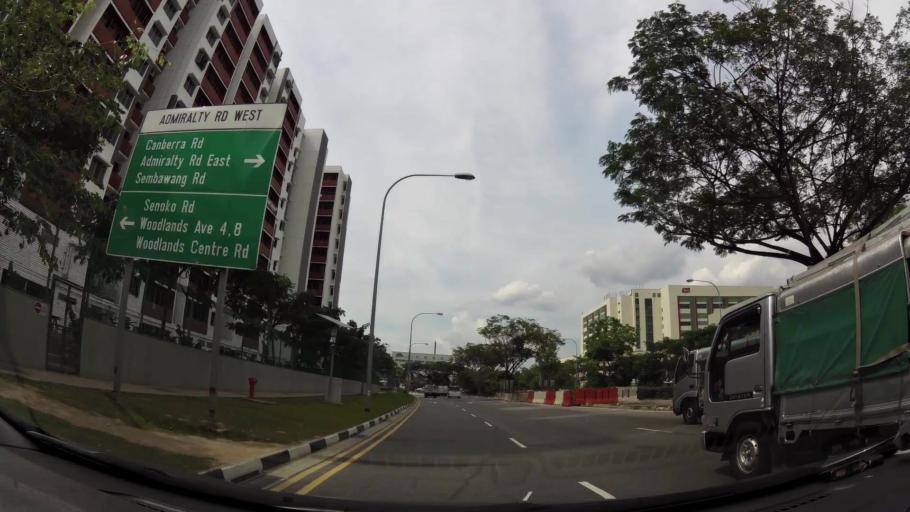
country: MY
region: Johor
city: Johor Bahru
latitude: 1.4614
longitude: 103.8100
